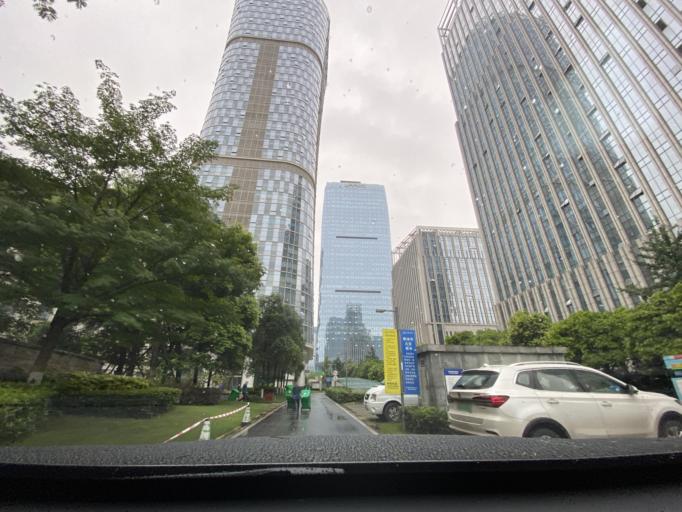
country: CN
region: Sichuan
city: Chengdu
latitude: 30.5433
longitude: 104.0614
